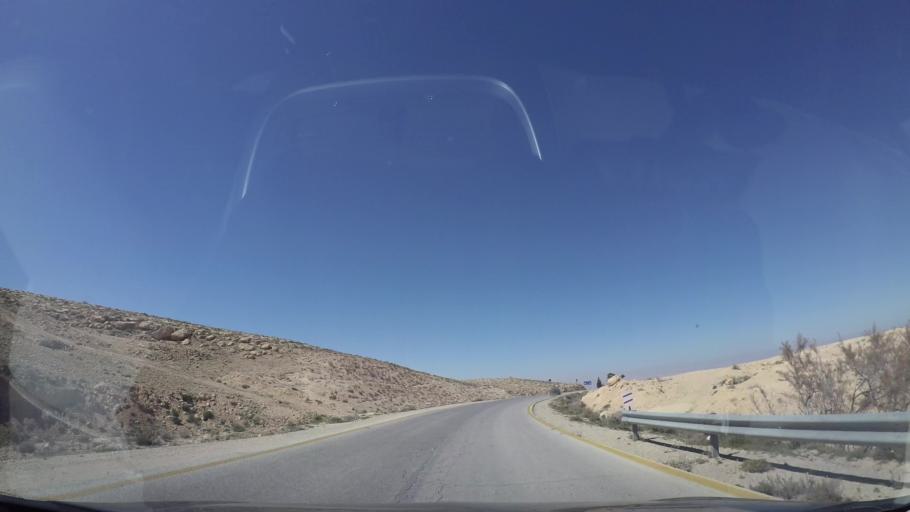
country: JO
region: Tafielah
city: At Tafilah
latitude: 30.8589
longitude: 35.5411
